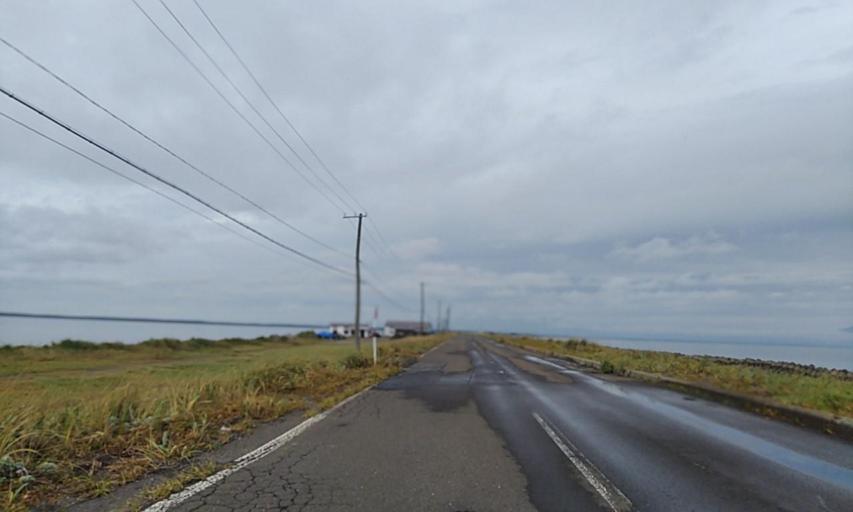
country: JP
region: Hokkaido
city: Shibetsu
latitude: 43.6122
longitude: 145.2608
